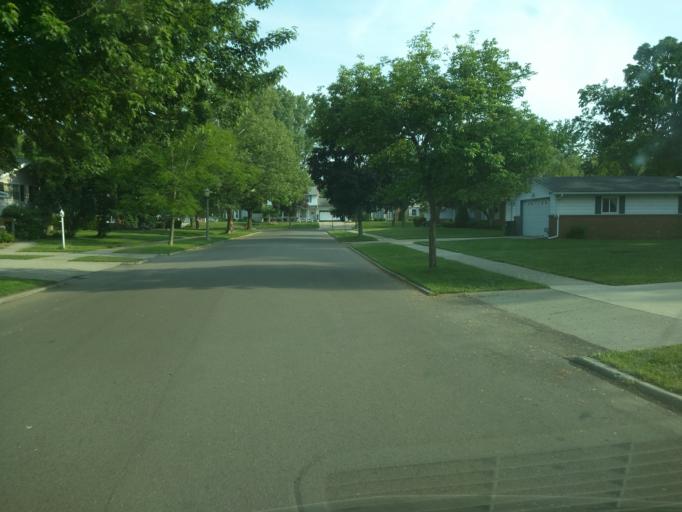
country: US
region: Michigan
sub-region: Ingham County
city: Edgemont Park
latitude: 42.7061
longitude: -84.5907
